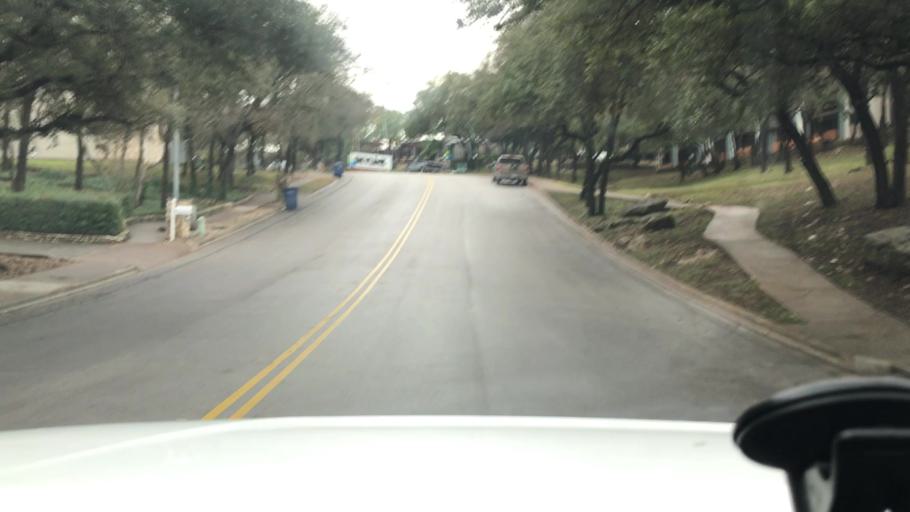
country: US
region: Texas
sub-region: Travis County
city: Rollingwood
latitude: 30.2622
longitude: -97.7859
